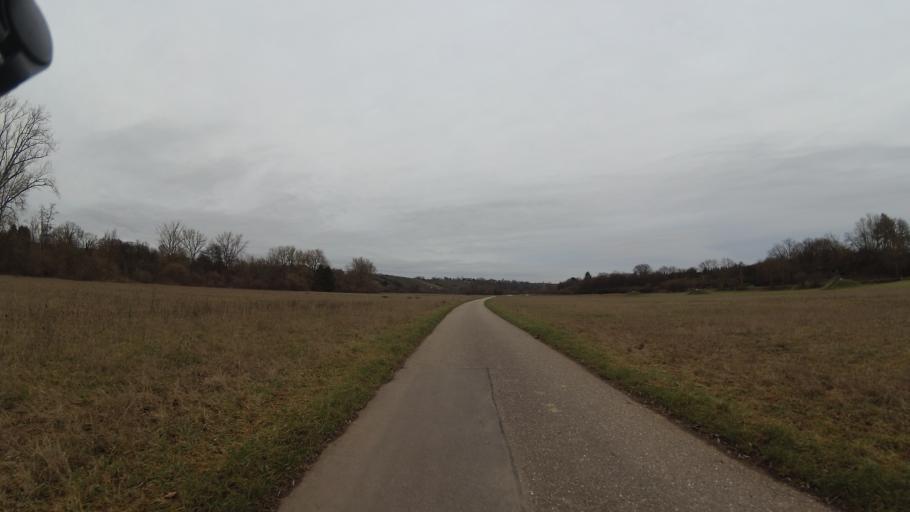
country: DE
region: Baden-Wuerttemberg
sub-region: Regierungsbezirk Stuttgart
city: Oedheim
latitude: 49.2472
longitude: 9.2608
